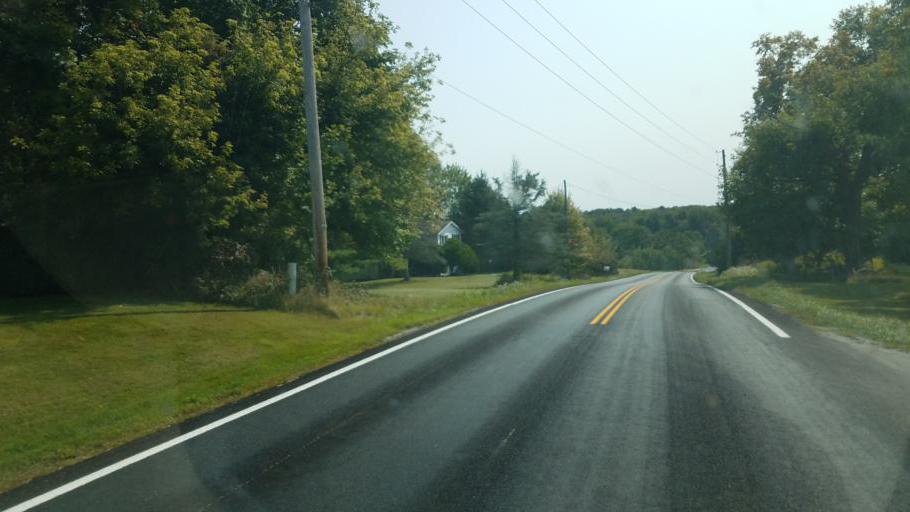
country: US
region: Ohio
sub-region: Sandusky County
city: Bellville
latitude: 40.5720
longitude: -82.5691
